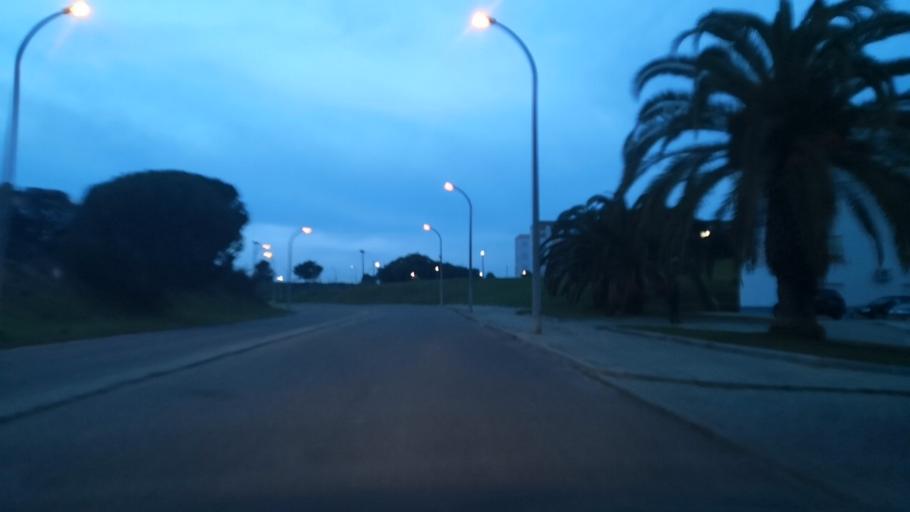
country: PT
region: Setubal
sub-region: Setubal
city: Setubal
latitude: 38.5208
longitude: -8.8603
